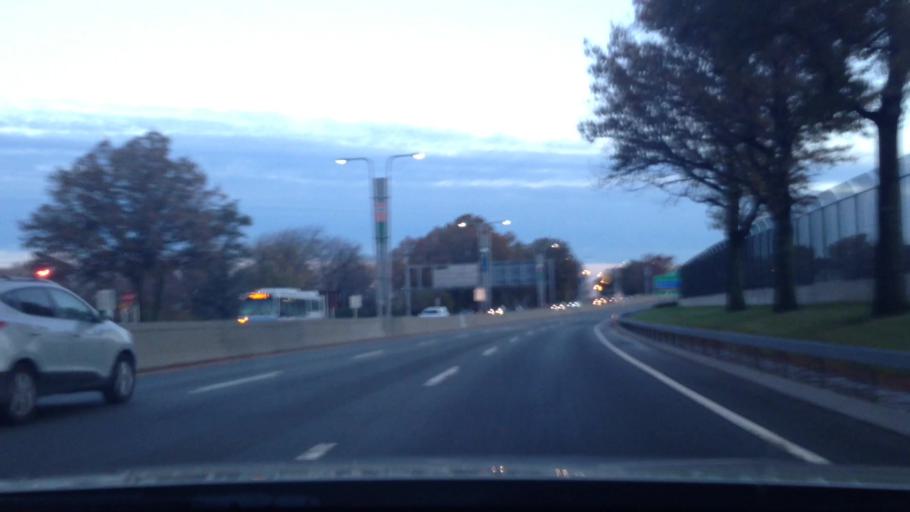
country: US
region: New York
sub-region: Queens County
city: Jamaica
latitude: 40.6538
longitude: -73.8069
